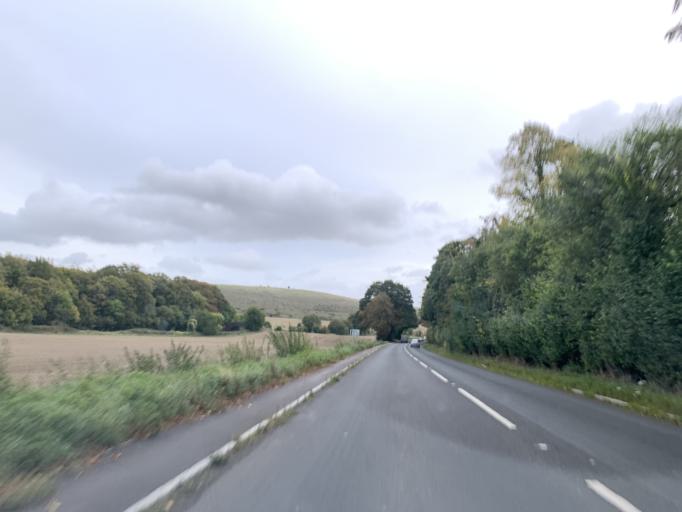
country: GB
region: England
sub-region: Wiltshire
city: Bishopstrow
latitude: 51.1923
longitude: -2.1319
